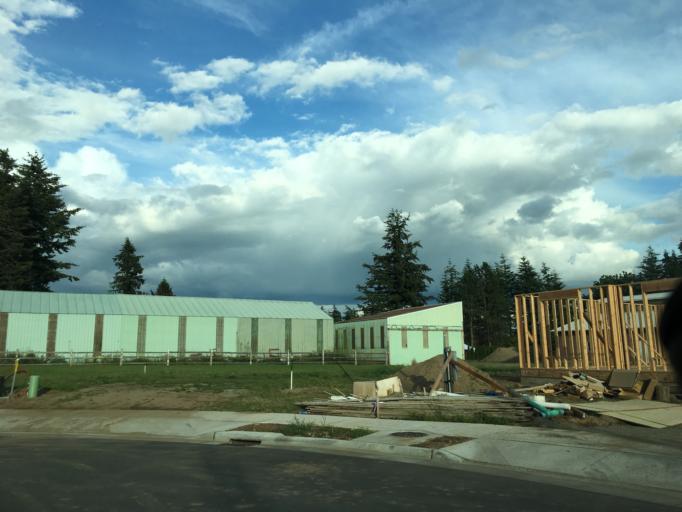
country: US
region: Washington
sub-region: Whatcom County
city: Lynden
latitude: 48.9607
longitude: -122.4094
